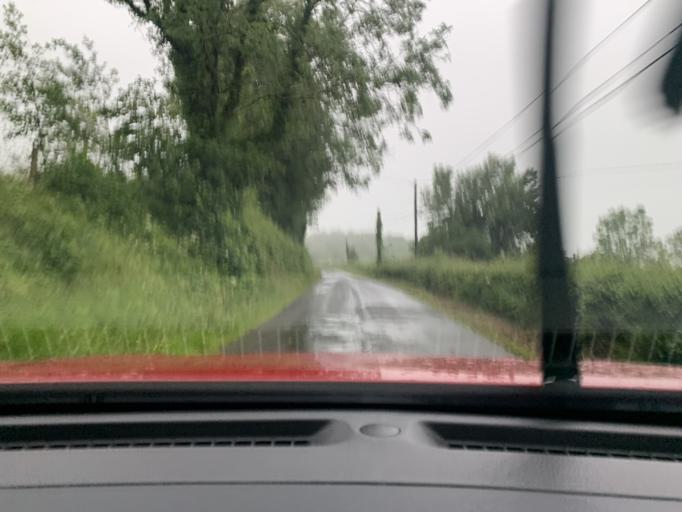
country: IE
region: Connaught
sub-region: Sligo
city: Sligo
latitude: 54.3251
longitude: -8.4232
